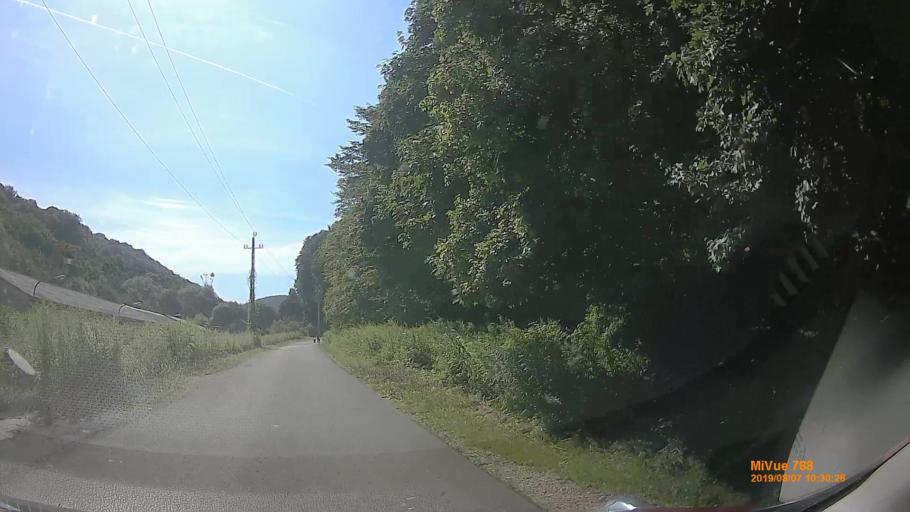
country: HU
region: Veszprem
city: Ajka
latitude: 47.0762
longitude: 17.5788
